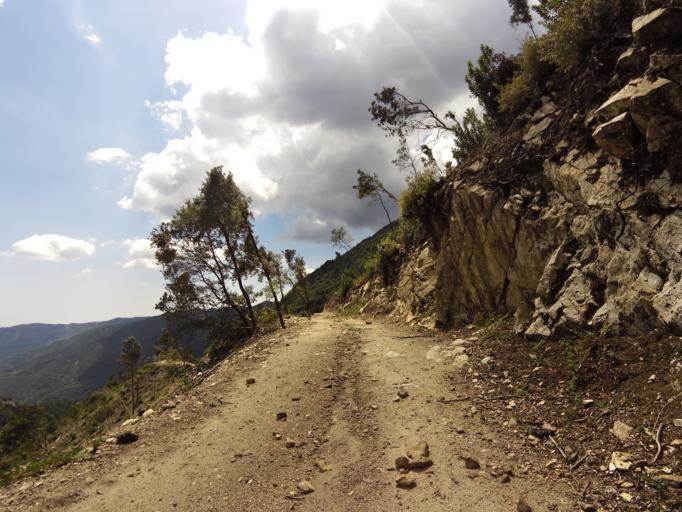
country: IT
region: Calabria
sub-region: Provincia di Vibo-Valentia
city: Nardodipace
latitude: 38.5047
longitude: 16.3941
